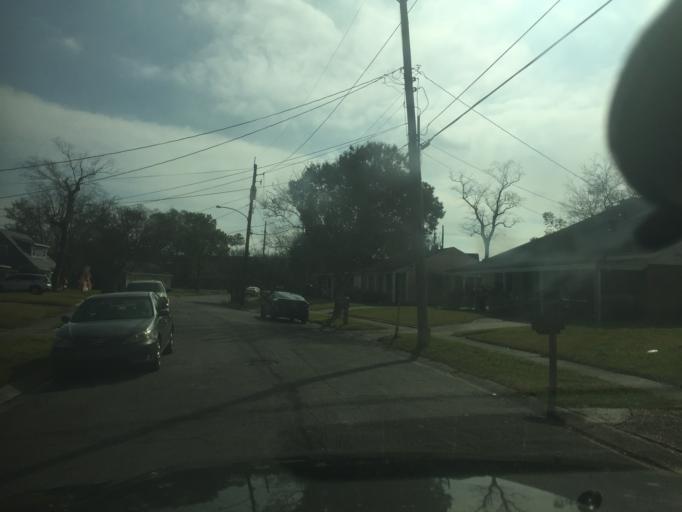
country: US
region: Louisiana
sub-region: Saint Bernard Parish
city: Arabi
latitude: 30.0072
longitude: -90.0397
